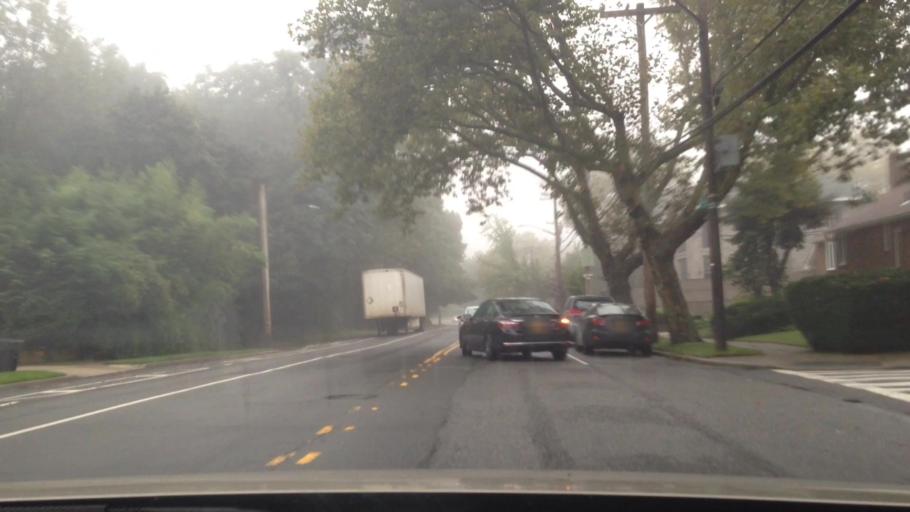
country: US
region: New York
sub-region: Nassau County
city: University Gardens
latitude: 40.7543
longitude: -73.7480
